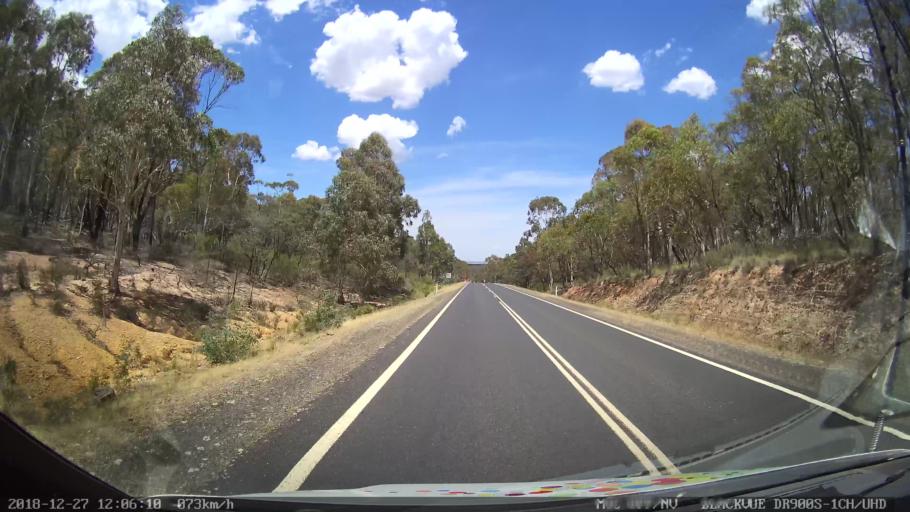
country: AU
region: New South Wales
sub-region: Blayney
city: Blayney
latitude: -33.8065
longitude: 149.3311
